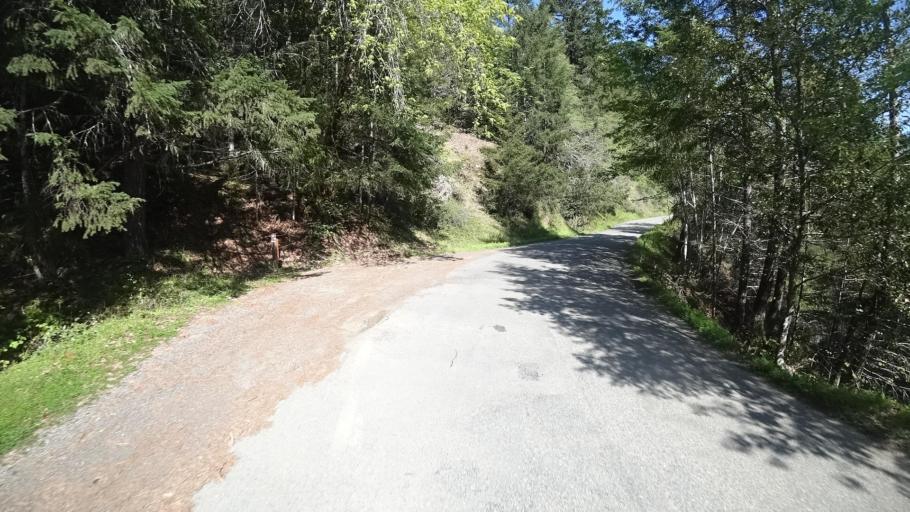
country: US
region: California
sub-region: Humboldt County
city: Redway
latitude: 40.0661
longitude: -123.6500
